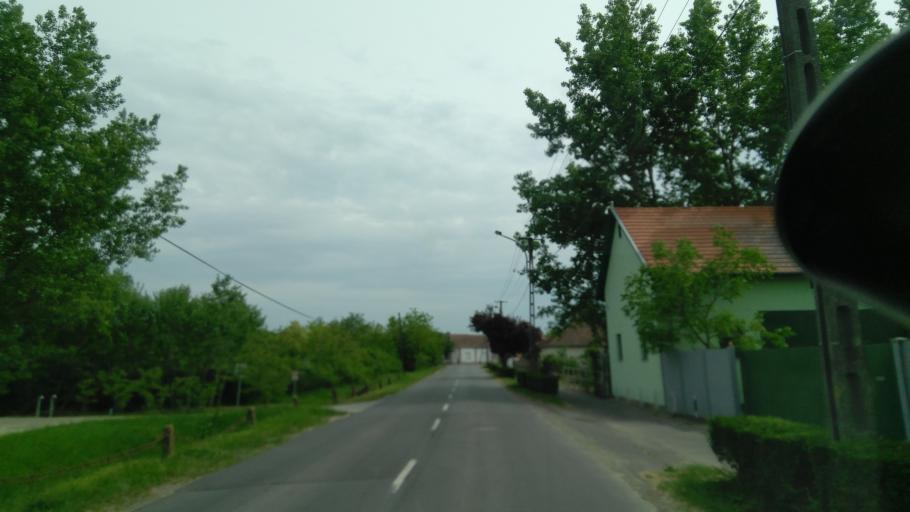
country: HU
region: Bekes
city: Sarkad
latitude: 46.8123
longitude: 21.3831
